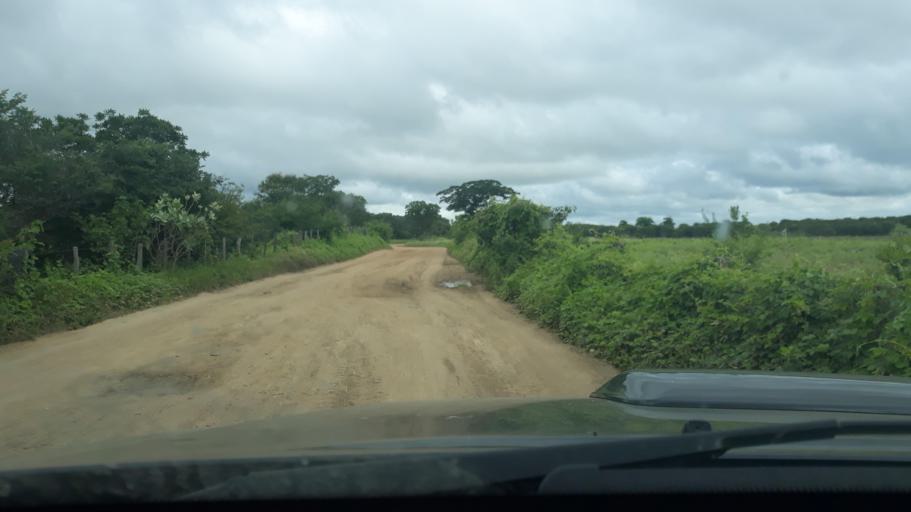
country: BR
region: Bahia
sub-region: Riacho De Santana
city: Riacho de Santana
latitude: -13.9001
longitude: -42.8714
